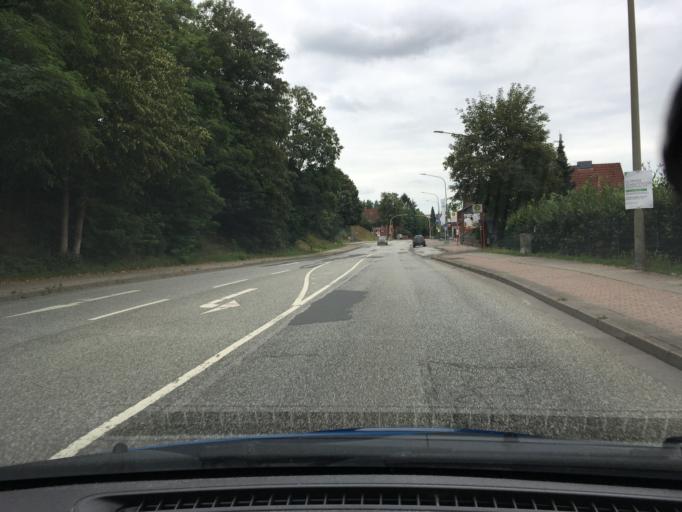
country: DE
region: Schleswig-Holstein
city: Geesthacht
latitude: 53.4511
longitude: 10.3580
